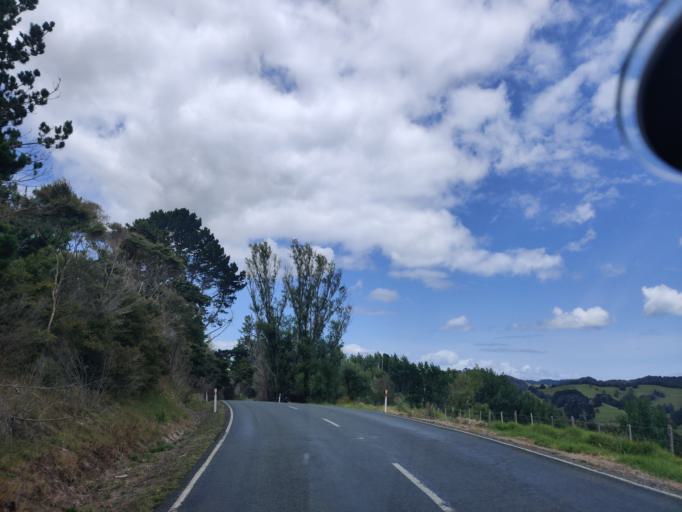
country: NZ
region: Northland
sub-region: Far North District
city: Kaitaia
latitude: -35.2793
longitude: 173.4840
